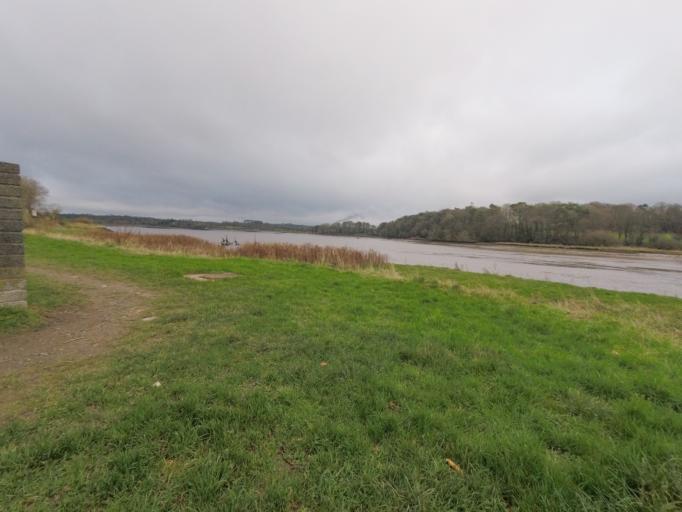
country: IE
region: Munster
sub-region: Waterford
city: Waterford
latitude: 52.2505
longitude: -7.0679
